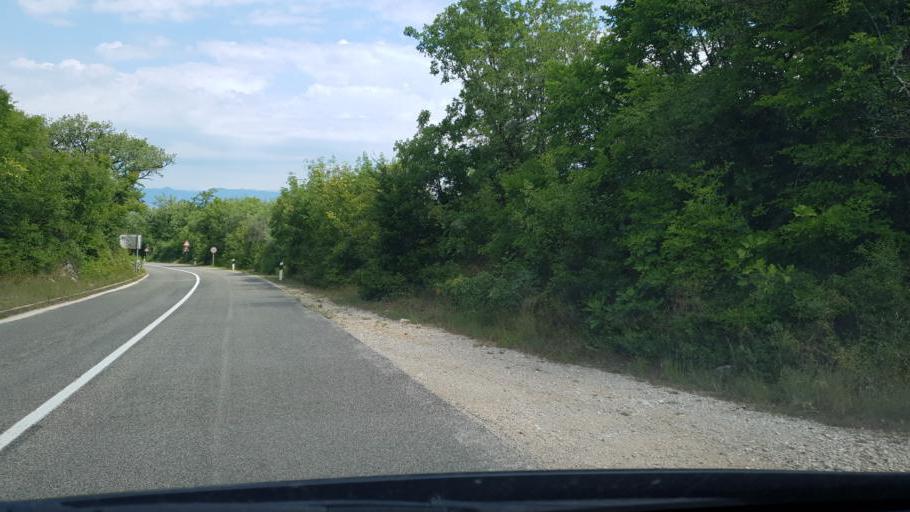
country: HR
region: Primorsko-Goranska
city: Njivice
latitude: 45.1346
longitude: 14.5841
